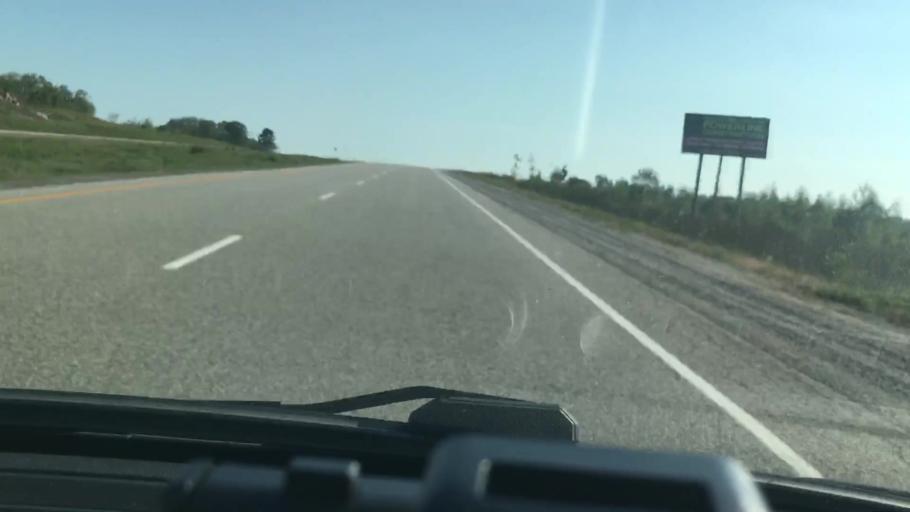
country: CA
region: Ontario
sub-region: Algoma
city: Sault Ste. Marie
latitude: 46.4625
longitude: -84.0592
